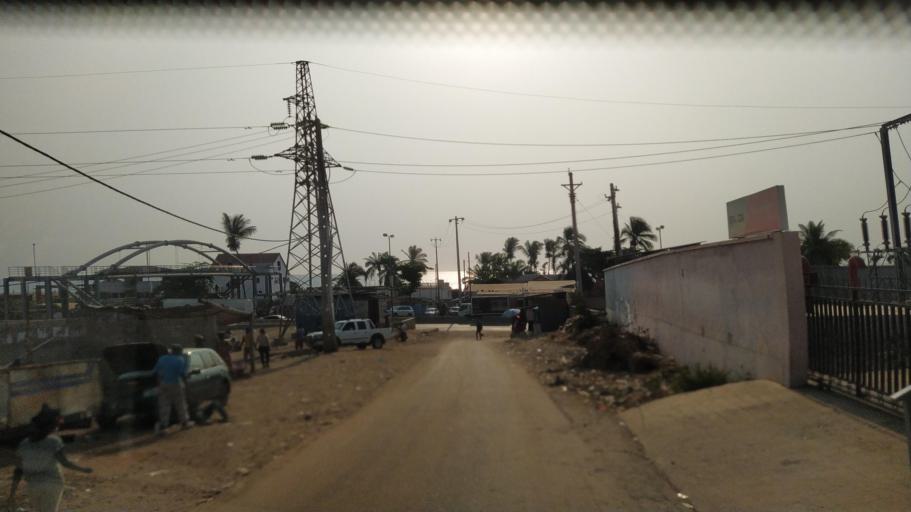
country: AO
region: Luanda
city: Luanda
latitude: -8.8707
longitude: 13.1975
